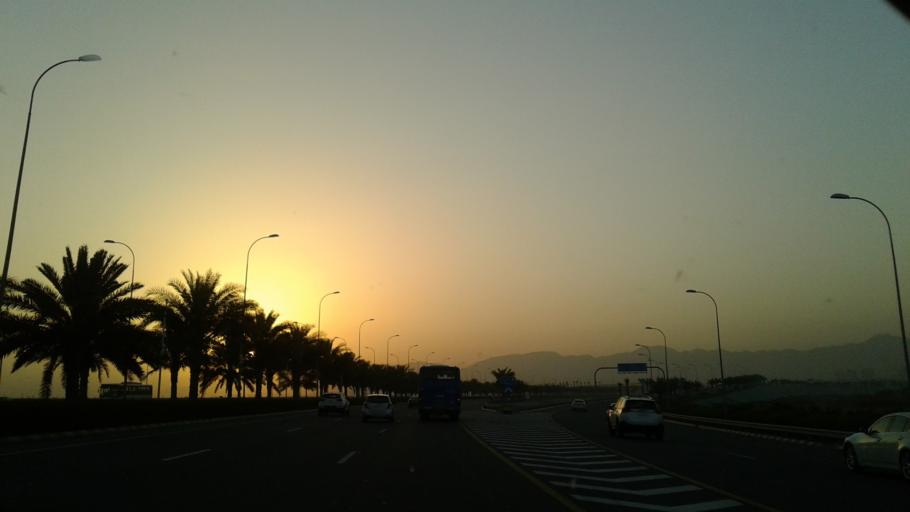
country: OM
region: Muhafazat Masqat
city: Bawshar
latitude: 23.6023
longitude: 58.3233
